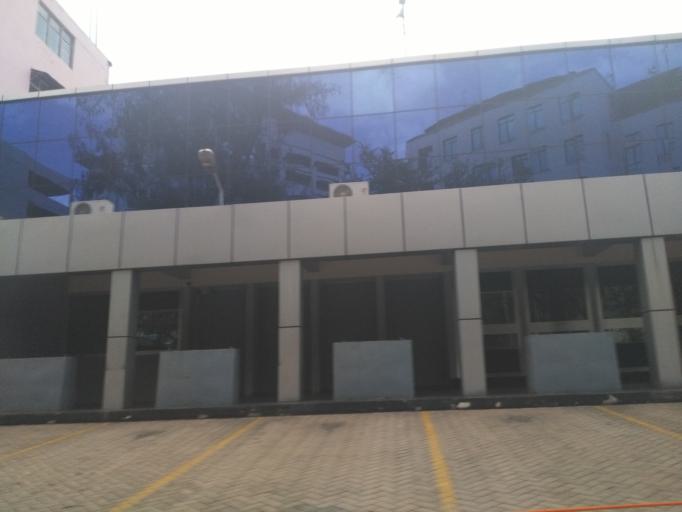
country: TZ
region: Dar es Salaam
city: Dar es Salaam
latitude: -6.8114
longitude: 39.2868
